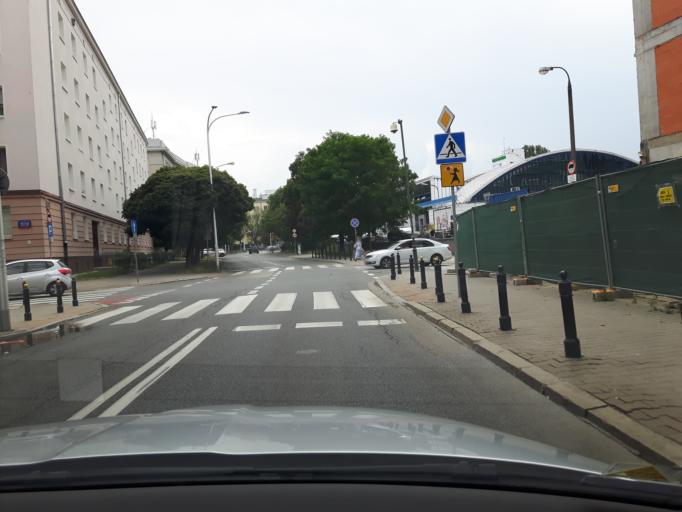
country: PL
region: Masovian Voivodeship
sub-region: Warszawa
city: Ochota
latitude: 52.2191
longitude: 20.9777
